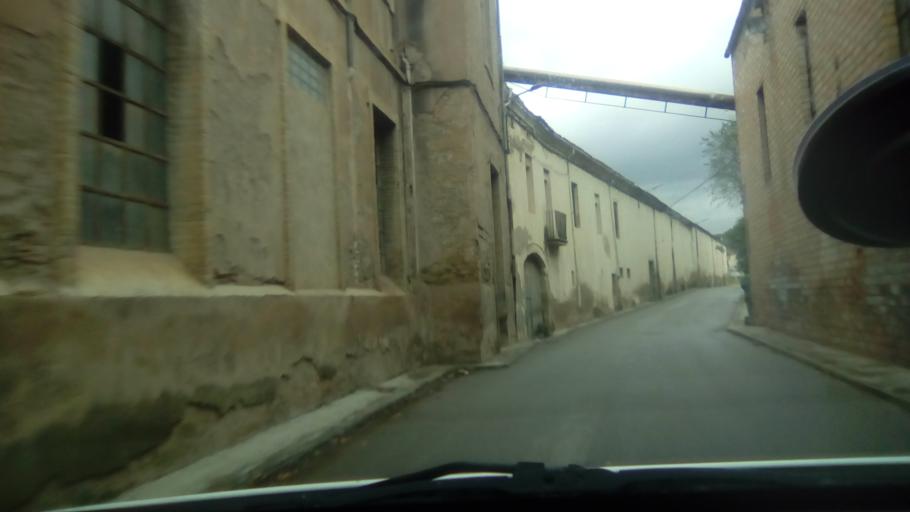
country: ES
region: Catalonia
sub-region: Provincia de Barcelona
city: Sant Fruitos de Bages
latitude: 41.6995
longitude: 1.8704
